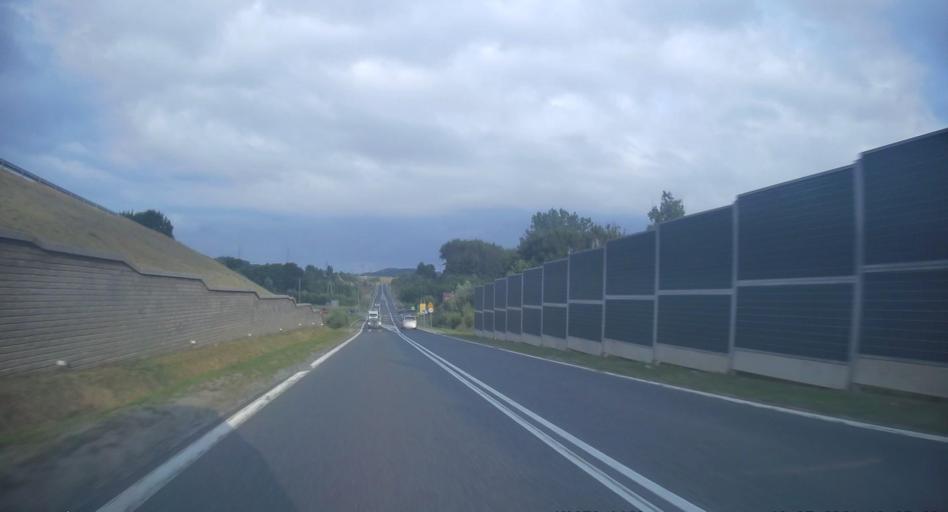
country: PL
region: Lower Silesian Voivodeship
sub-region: Powiat klodzki
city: Nowa Ruda
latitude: 50.6043
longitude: 16.5048
